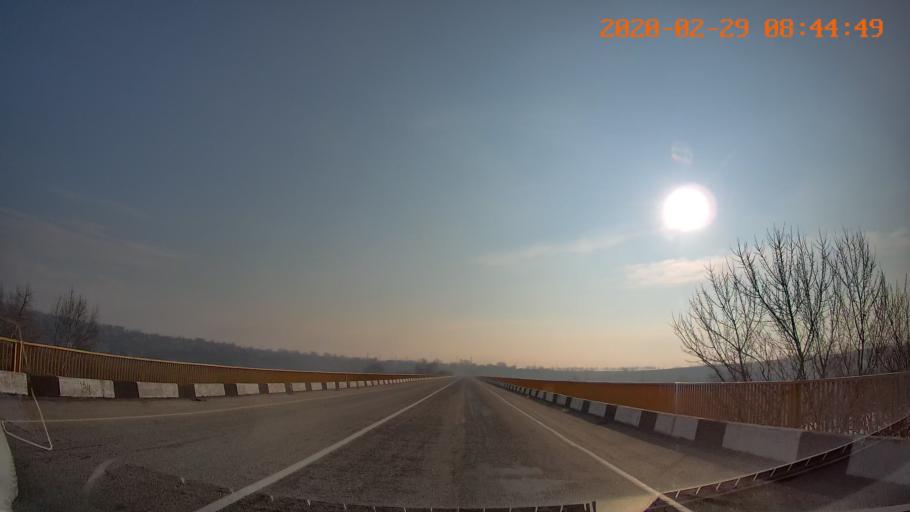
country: MD
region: Anenii Noi
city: Varnita
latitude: 46.9199
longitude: 29.4708
